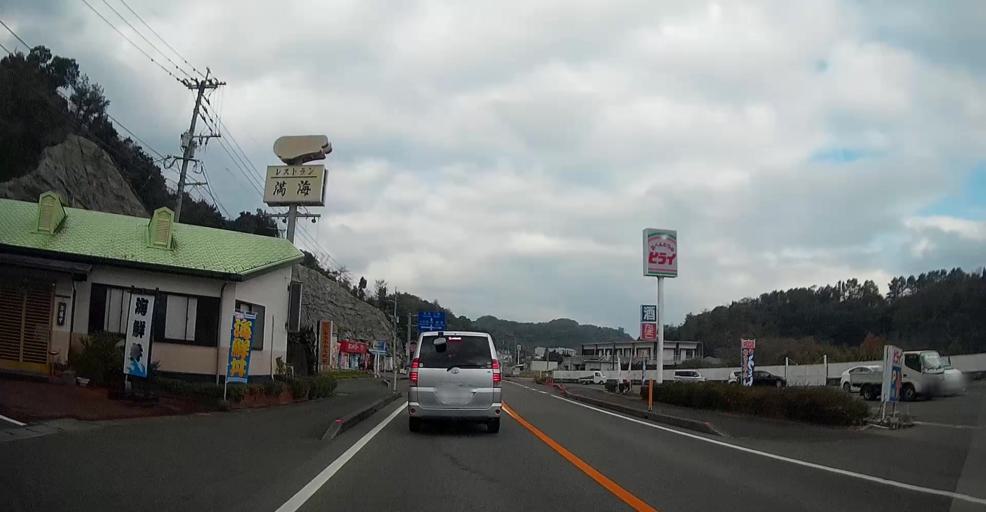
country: JP
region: Kumamoto
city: Yatsushiro
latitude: 32.5515
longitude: 130.4191
